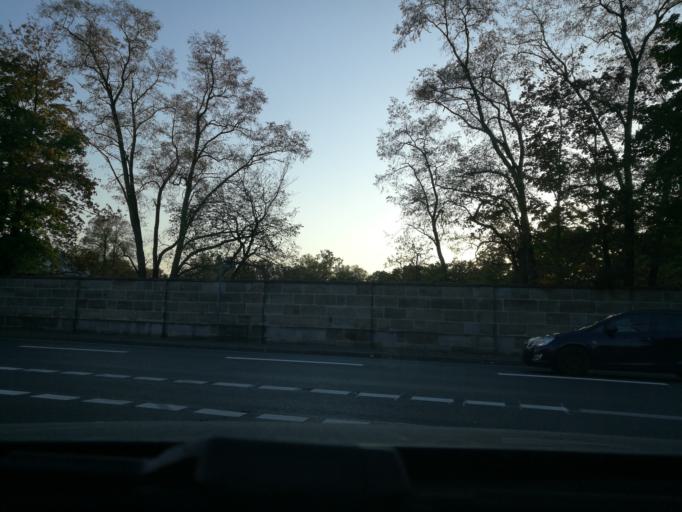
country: DE
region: Bavaria
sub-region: Regierungsbezirk Mittelfranken
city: Furth
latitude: 49.4881
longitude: 10.9941
